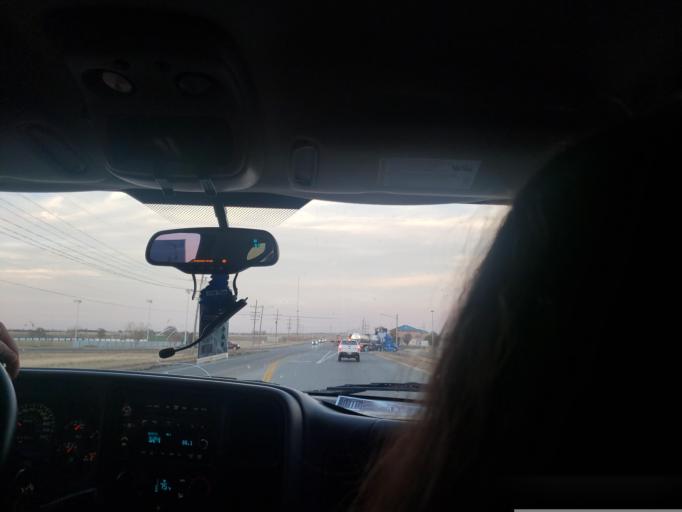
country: US
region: Kansas
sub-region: Seward County
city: Liberal
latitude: 37.0506
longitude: -100.9042
